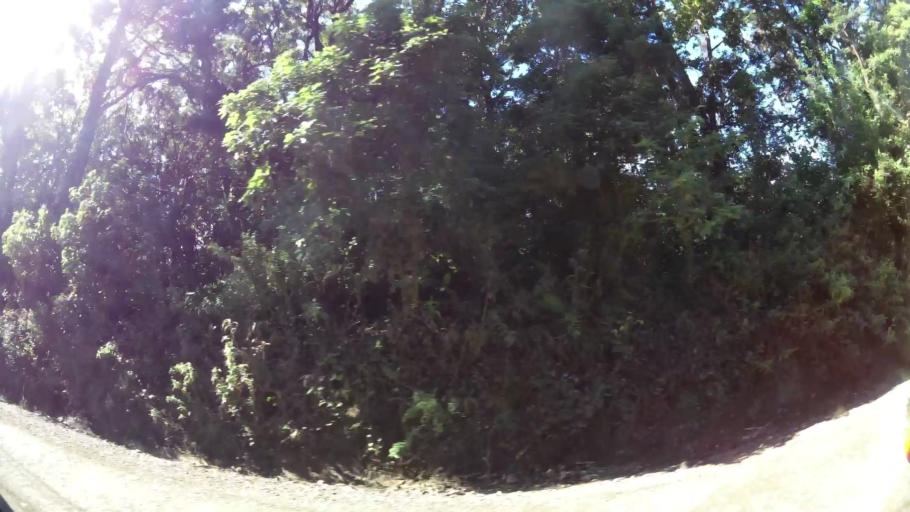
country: CR
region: Guanacaste
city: Juntas
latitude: 10.3264
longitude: -84.8366
